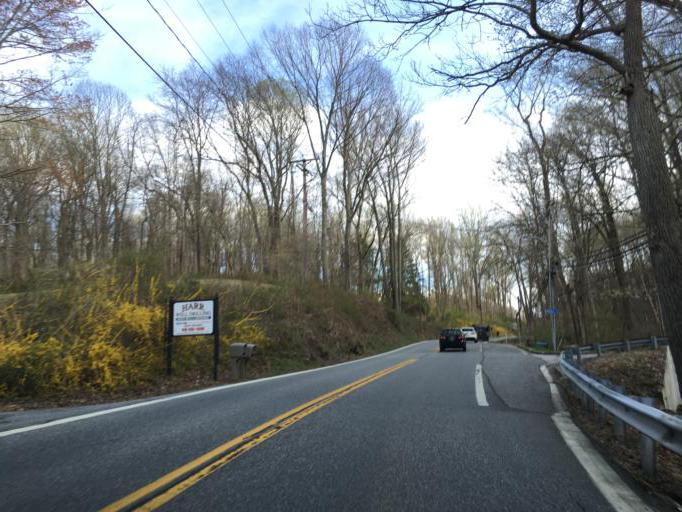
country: US
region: Maryland
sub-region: Baltimore County
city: Mays Chapel
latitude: 39.4568
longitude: -76.6920
